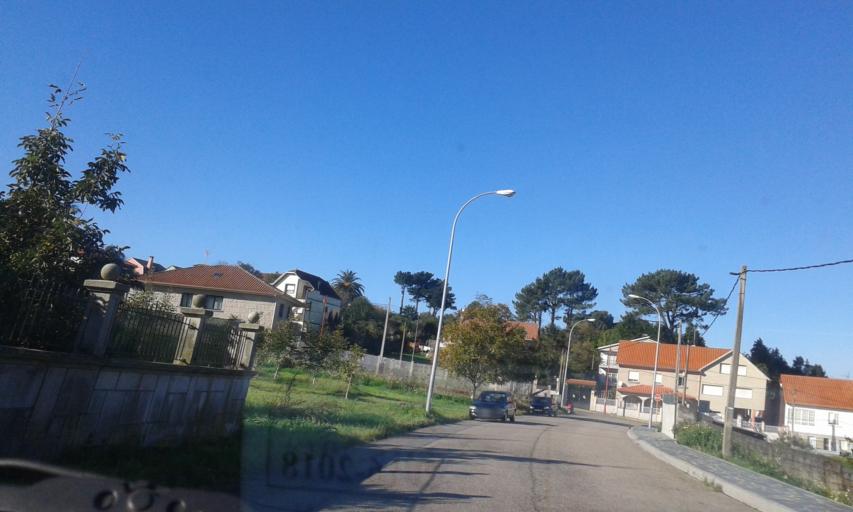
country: ES
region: Galicia
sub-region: Provincia de Pontevedra
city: Marin
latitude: 42.3726
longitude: -8.7353
